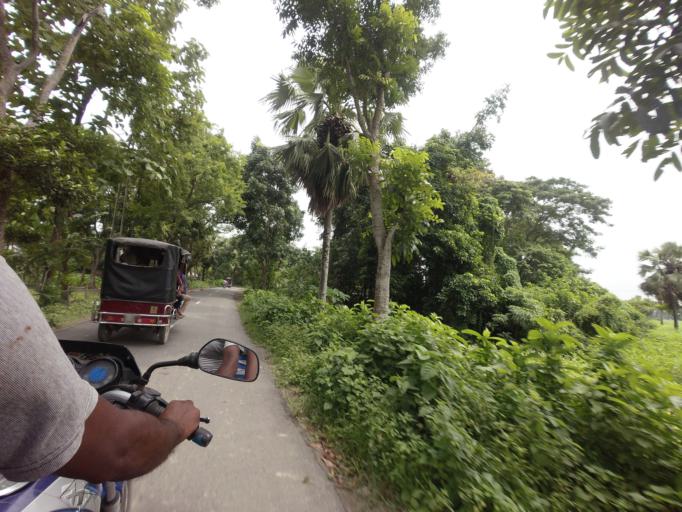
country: BD
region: Khulna
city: Kalia
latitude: 23.0932
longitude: 89.6550
